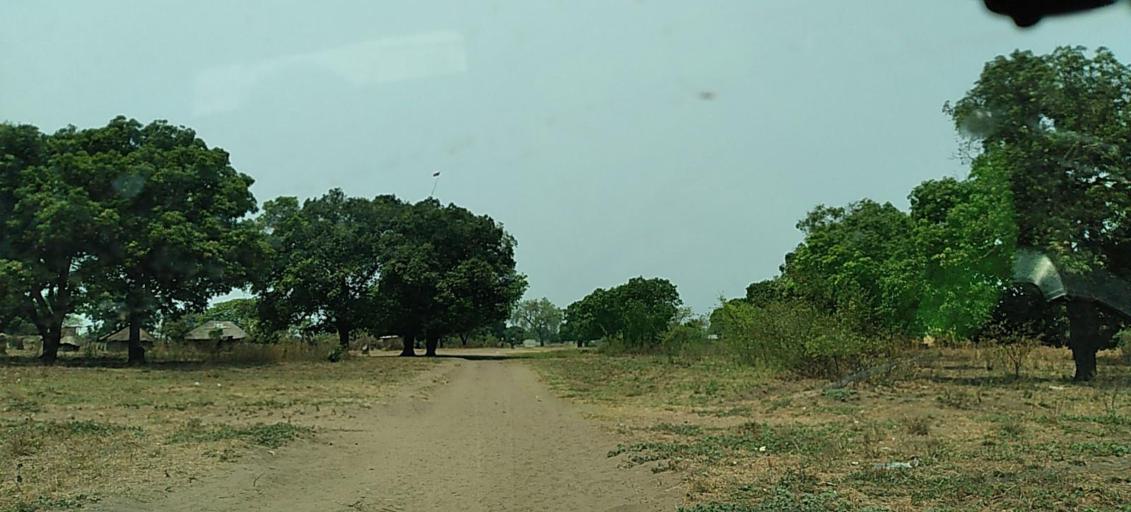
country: ZM
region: Western
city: Lukulu
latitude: -14.1594
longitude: 23.3161
